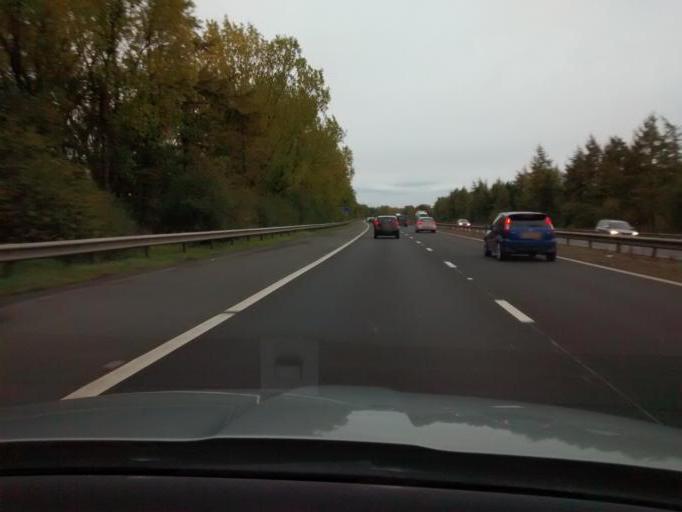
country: GB
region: Scotland
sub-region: Falkirk
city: Grangemouth
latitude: 56.0170
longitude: -3.7512
